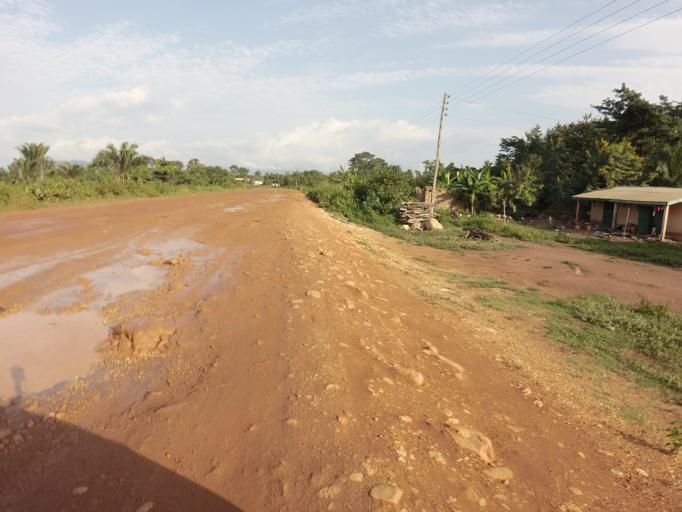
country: GH
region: Volta
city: Kpandu
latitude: 7.0082
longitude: 0.4295
